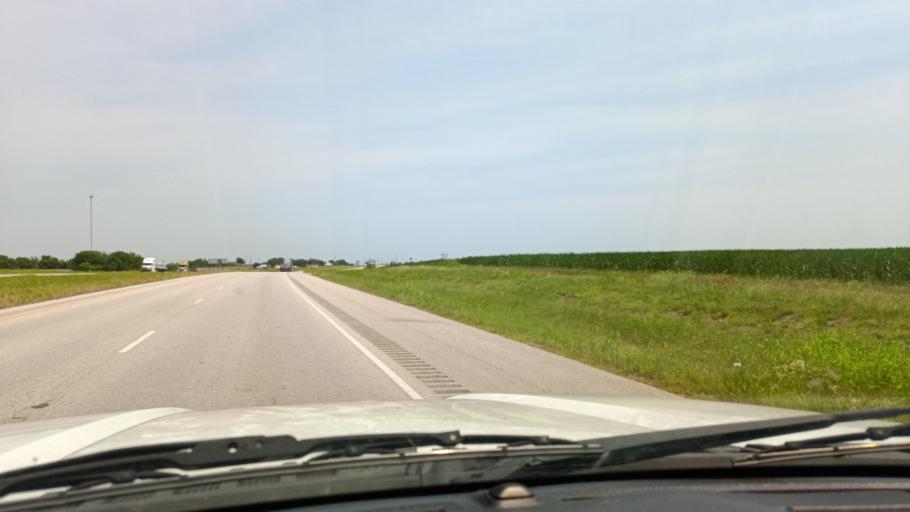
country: US
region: Texas
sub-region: Bell County
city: Little River-Academy
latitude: 31.0075
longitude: -97.2954
